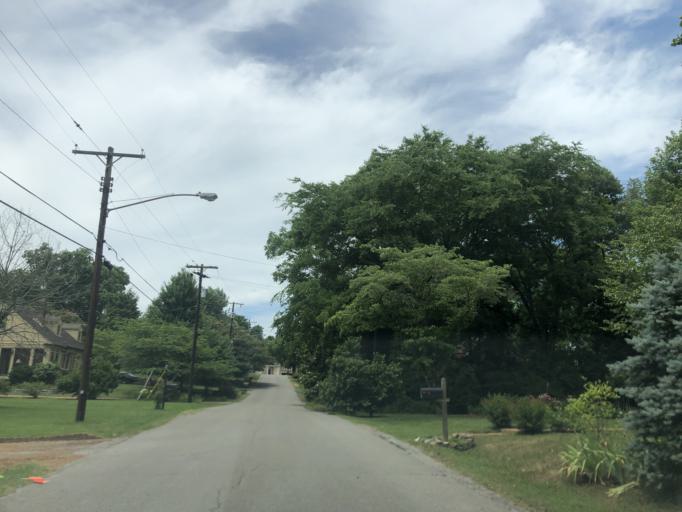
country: US
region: Tennessee
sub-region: Davidson County
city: Oak Hill
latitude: 36.1012
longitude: -86.7962
